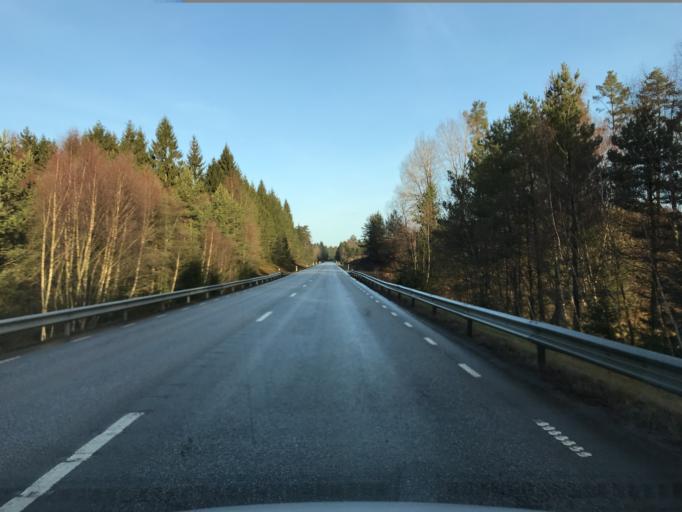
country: SE
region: Skane
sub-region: Hassleholms Kommun
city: Bjarnum
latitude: 56.2257
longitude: 13.7213
